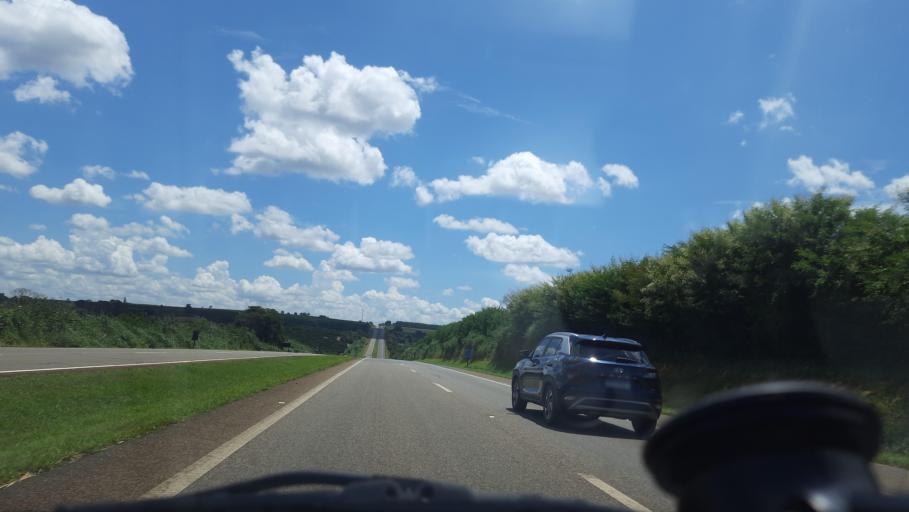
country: BR
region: Sao Paulo
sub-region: Aguai
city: Aguai
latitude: -21.9672
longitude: -47.0433
